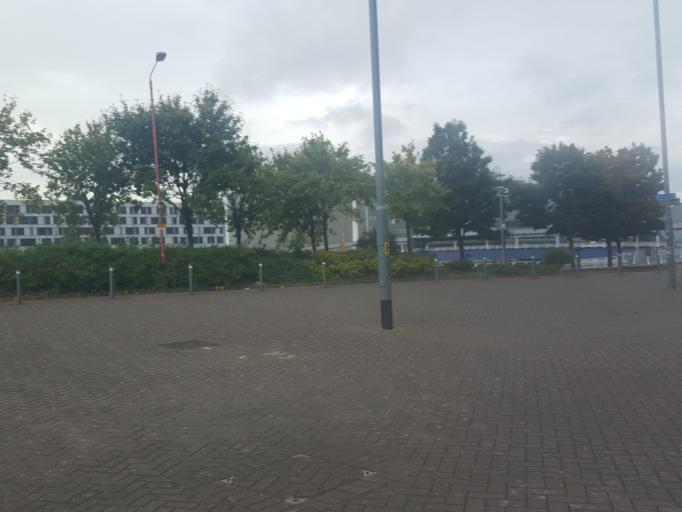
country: GB
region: Scotland
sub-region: Glasgow City
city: Glasgow
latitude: 55.8593
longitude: -4.2874
